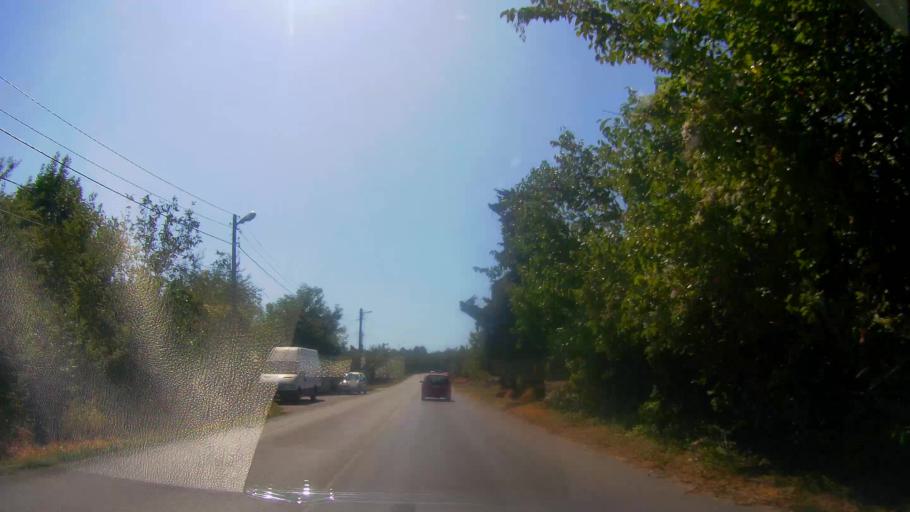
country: BG
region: Veliko Turnovo
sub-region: Obshtina Gorna Oryakhovitsa
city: Purvomaytsi
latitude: 43.1718
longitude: 25.6206
